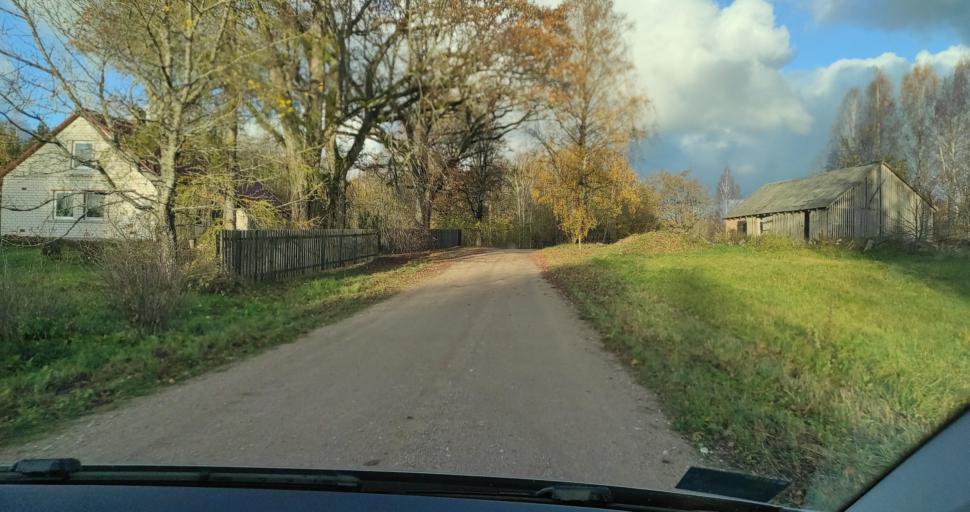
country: LV
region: Alsunga
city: Alsunga
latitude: 56.9497
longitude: 21.6308
